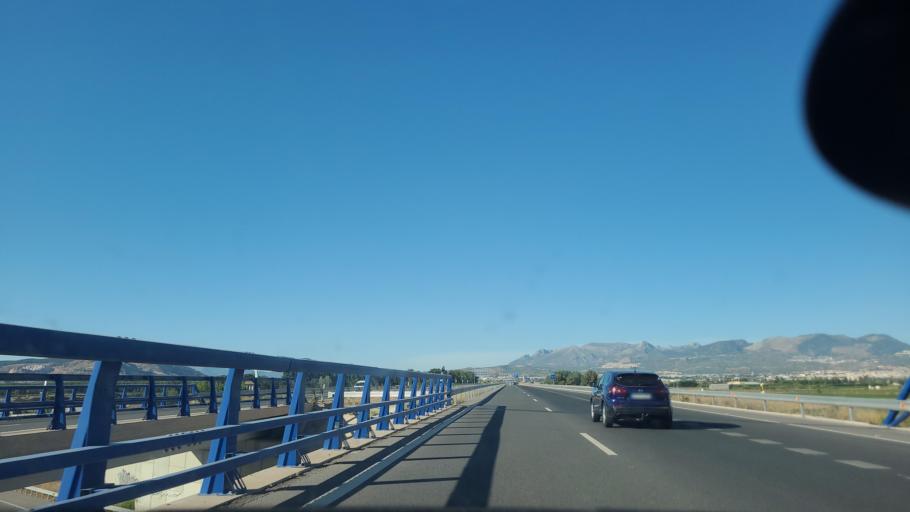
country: ES
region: Andalusia
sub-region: Provincia de Granada
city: Atarfe
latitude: 37.1857
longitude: -3.6957
